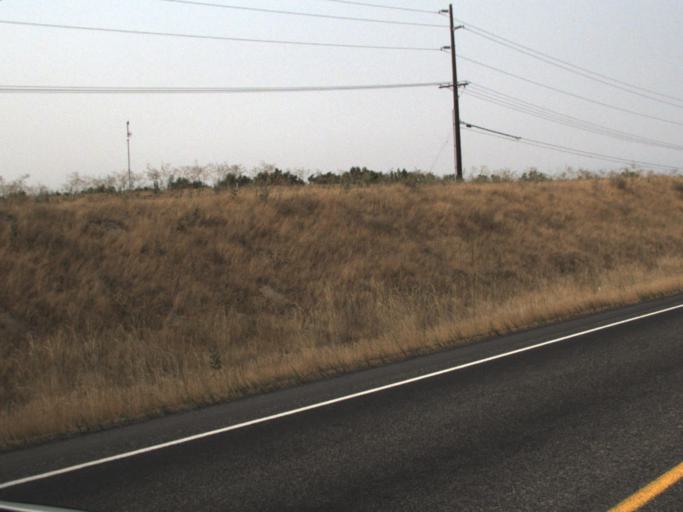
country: US
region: Oregon
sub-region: Morrow County
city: Irrigon
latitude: 45.9559
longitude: -119.6029
